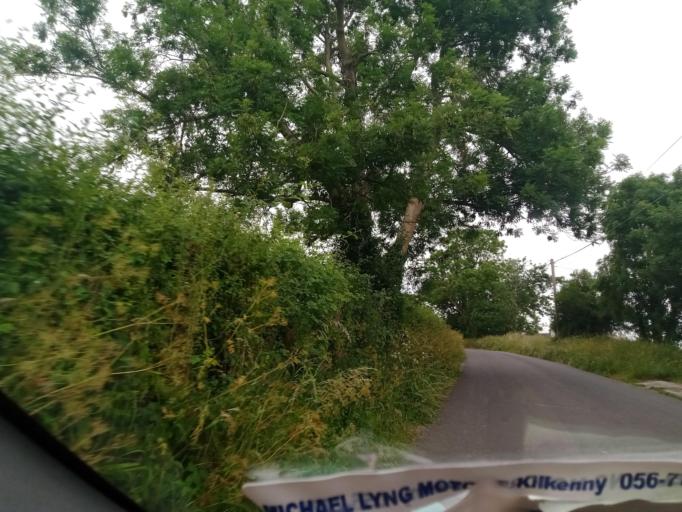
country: IE
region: Leinster
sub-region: Kilkenny
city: Ballyragget
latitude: 52.7504
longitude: -7.4319
